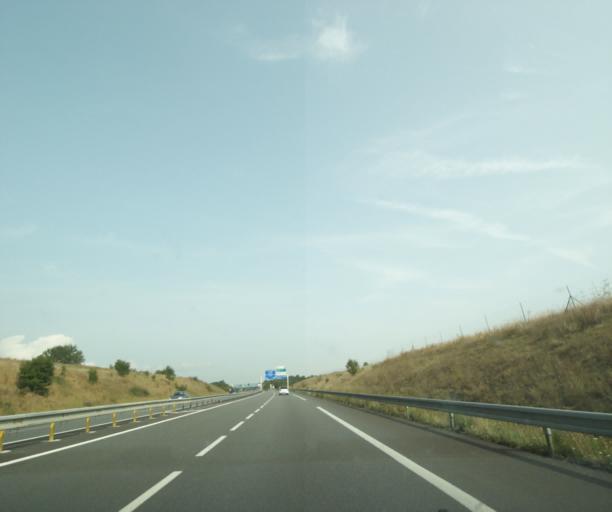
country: FR
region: Lower Normandy
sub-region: Departement de l'Orne
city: Valframbert
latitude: 48.4482
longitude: 0.1339
